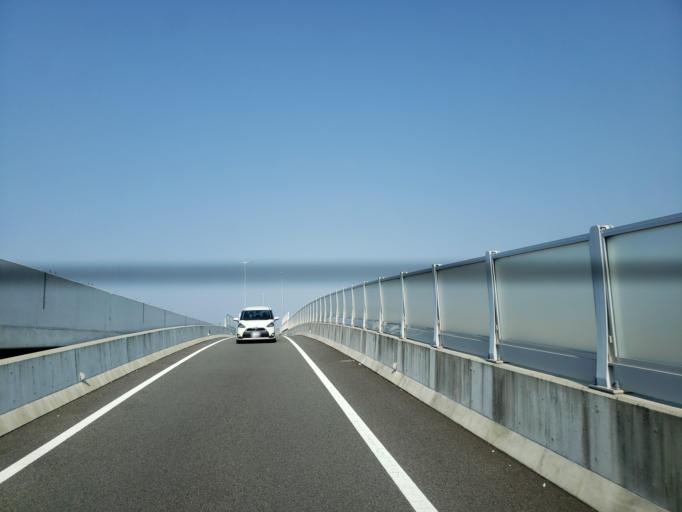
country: JP
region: Ehime
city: Masaki-cho
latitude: 33.8110
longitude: 132.7298
